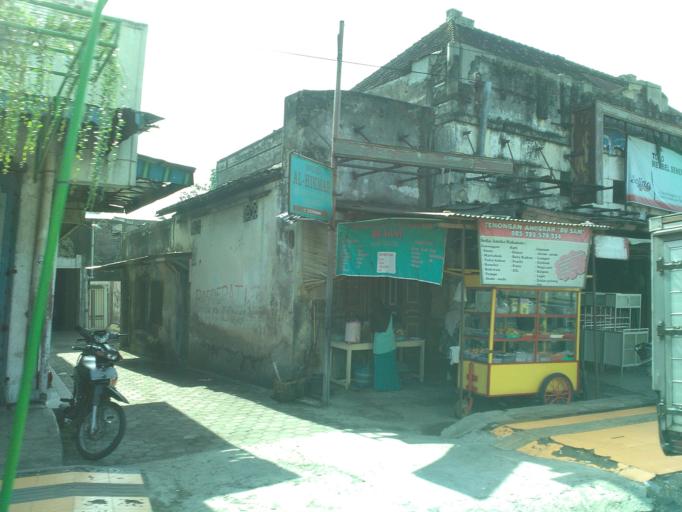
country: ID
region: Central Java
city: Delanggu
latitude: -7.6212
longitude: 110.6986
